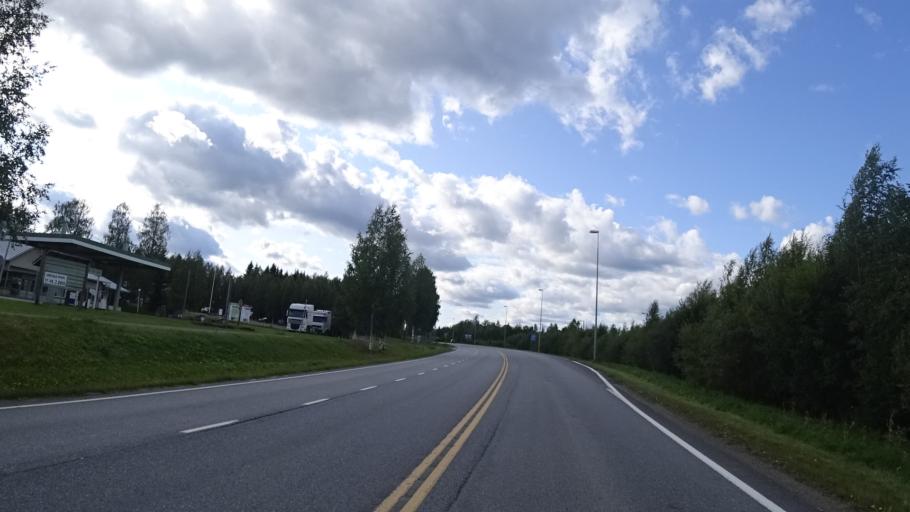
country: RU
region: Republic of Karelia
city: Vyartsilya
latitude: 62.1759
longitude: 30.5906
